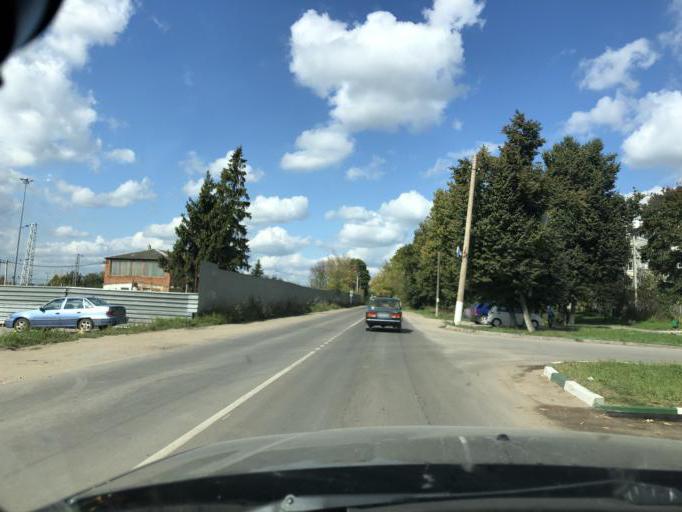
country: RU
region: Tula
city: Yasnogorsk
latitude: 54.4809
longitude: 37.6848
